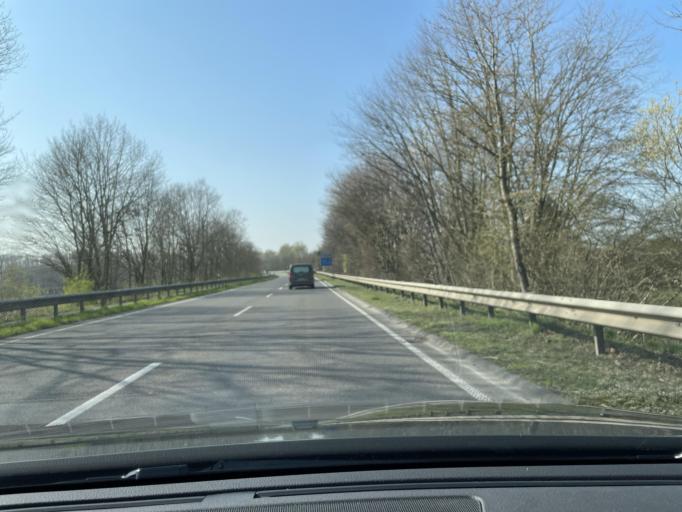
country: DE
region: North Rhine-Westphalia
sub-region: Regierungsbezirk Dusseldorf
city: Korschenbroich
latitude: 51.2210
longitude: 6.4990
